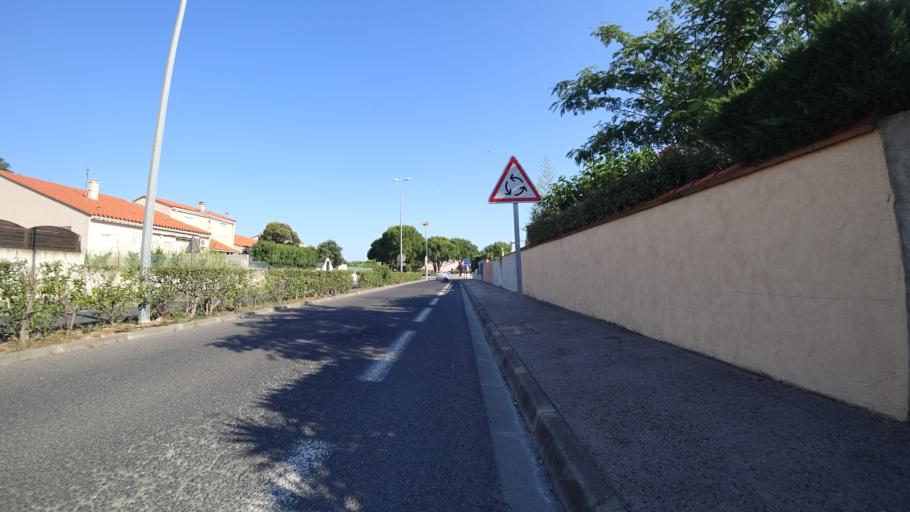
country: FR
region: Languedoc-Roussillon
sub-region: Departement des Pyrenees-Orientales
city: Cabestany
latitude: 42.6880
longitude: 2.9391
